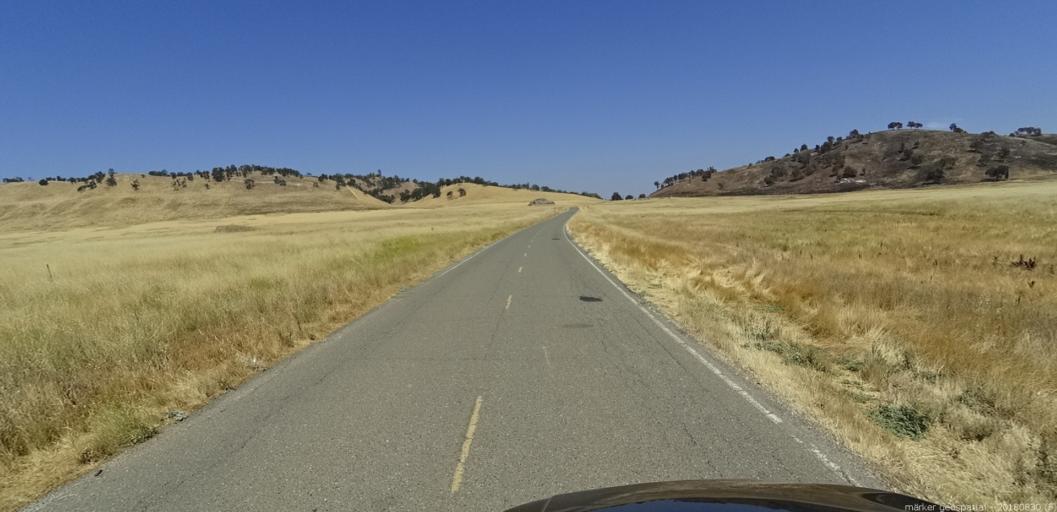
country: US
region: California
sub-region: Monterey County
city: King City
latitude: 35.9647
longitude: -121.2771
